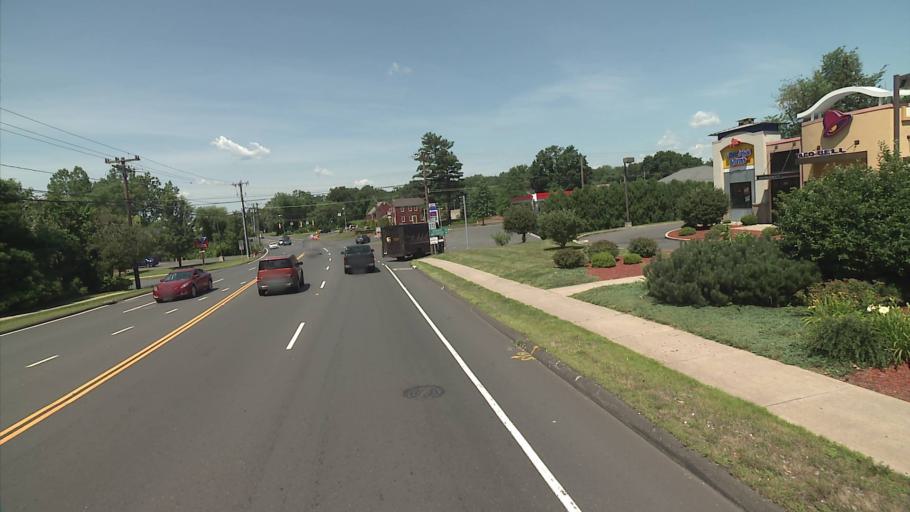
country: US
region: Connecticut
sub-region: Hartford County
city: Plainville
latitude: 41.6777
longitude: -72.8455
